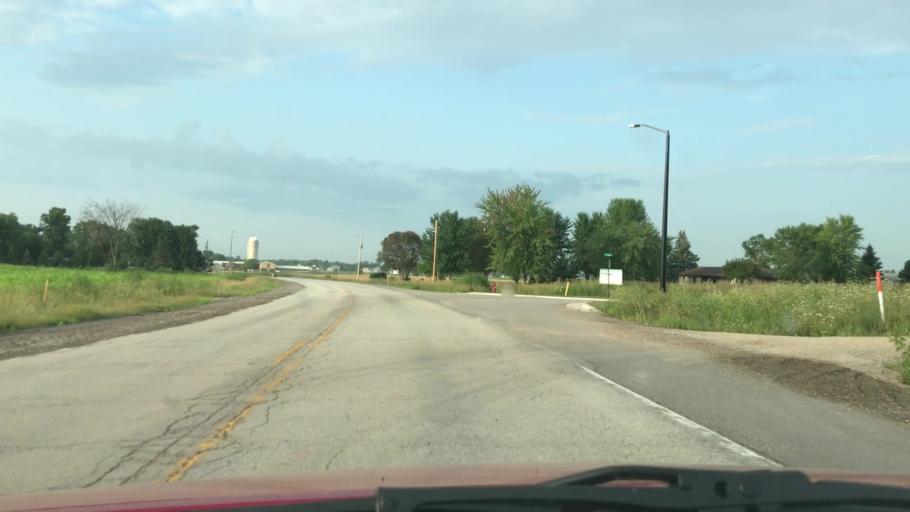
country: US
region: Wisconsin
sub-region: Brown County
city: De Pere
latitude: 44.4396
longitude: -88.1354
